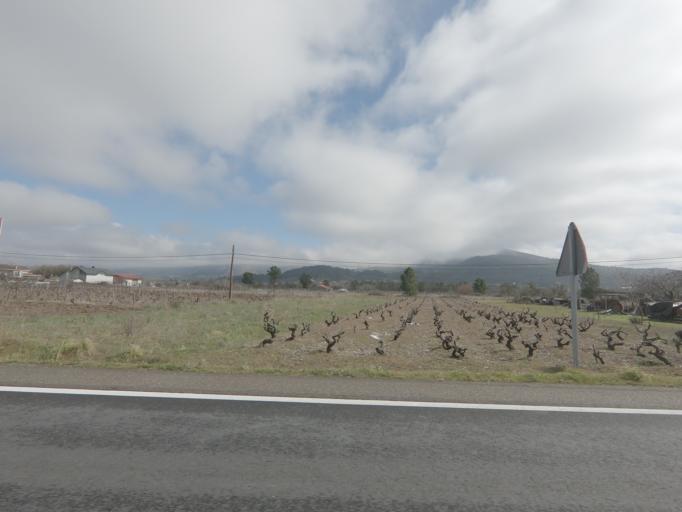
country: ES
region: Galicia
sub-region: Provincia de Ourense
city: Verin
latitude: 41.9158
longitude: -7.4433
